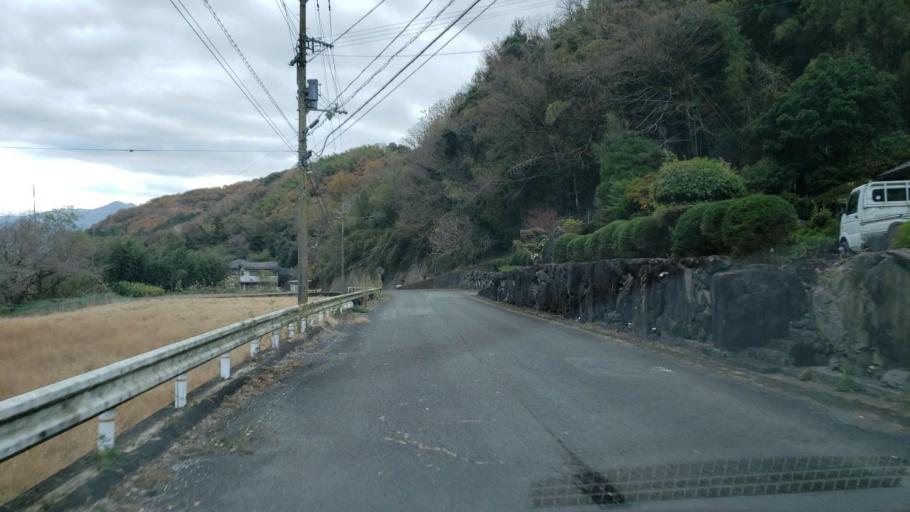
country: JP
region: Tokushima
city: Wakimachi
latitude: 34.1249
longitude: 134.2267
